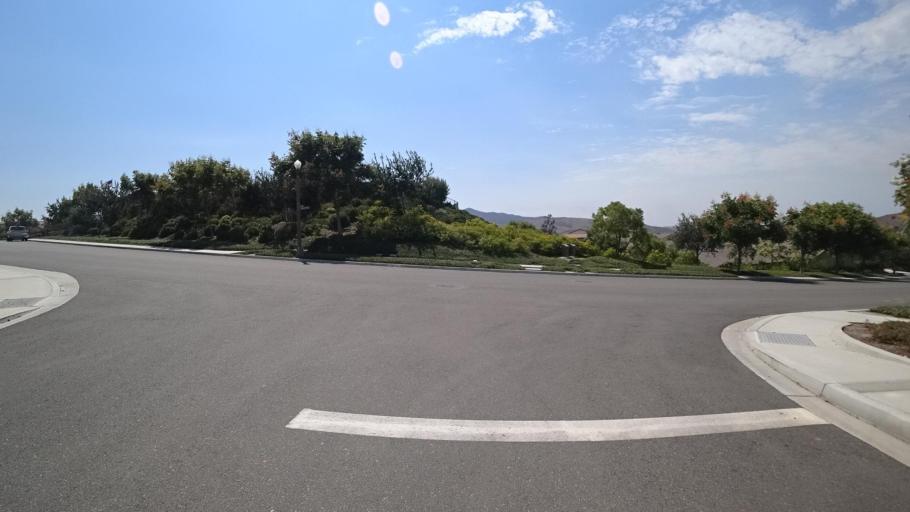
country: US
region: California
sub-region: Orange County
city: Ladera Ranch
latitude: 33.5368
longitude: -117.6053
